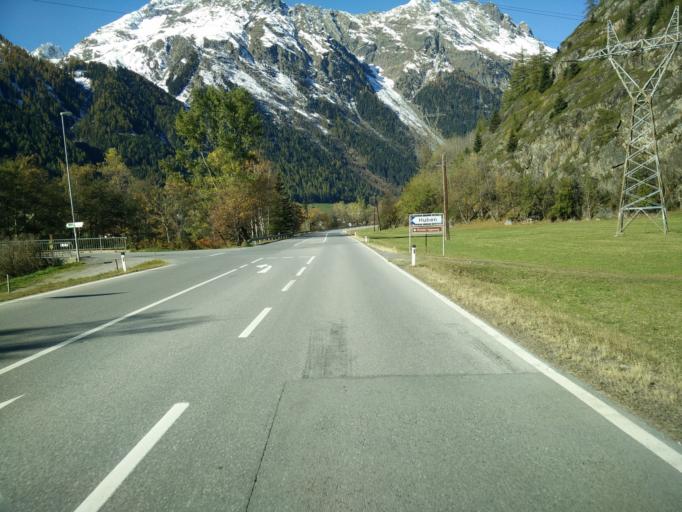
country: AT
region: Tyrol
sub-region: Politischer Bezirk Imst
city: Soelden
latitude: 47.0405
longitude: 10.9792
